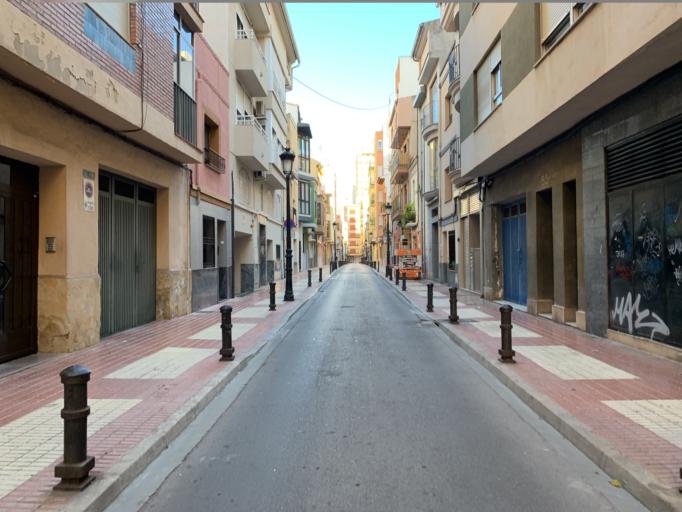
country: ES
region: Valencia
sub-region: Provincia de Castello
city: Castello de la Plana
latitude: 39.9854
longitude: -0.0433
